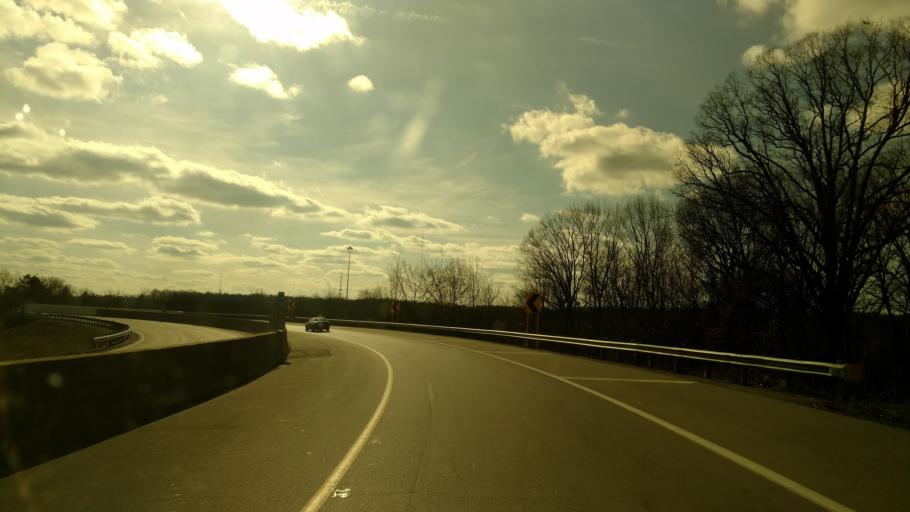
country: US
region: Ohio
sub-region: Summit County
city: Akron
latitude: 41.0618
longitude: -81.5666
